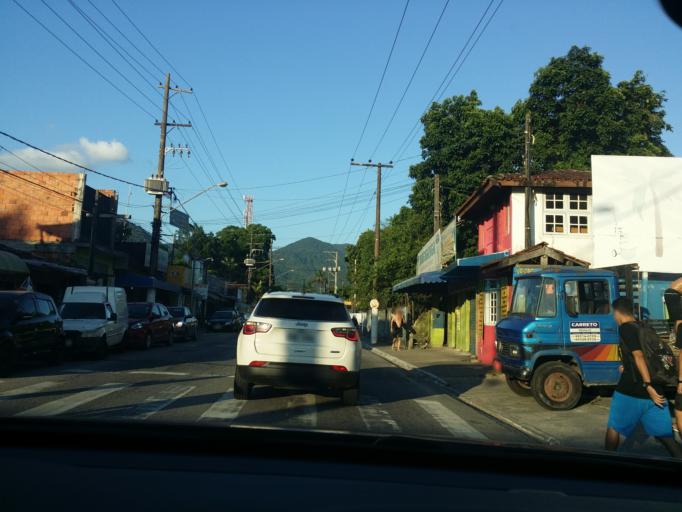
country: BR
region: Sao Paulo
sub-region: Sao Sebastiao
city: Sao Sebastiao
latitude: -23.7853
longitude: -45.6242
